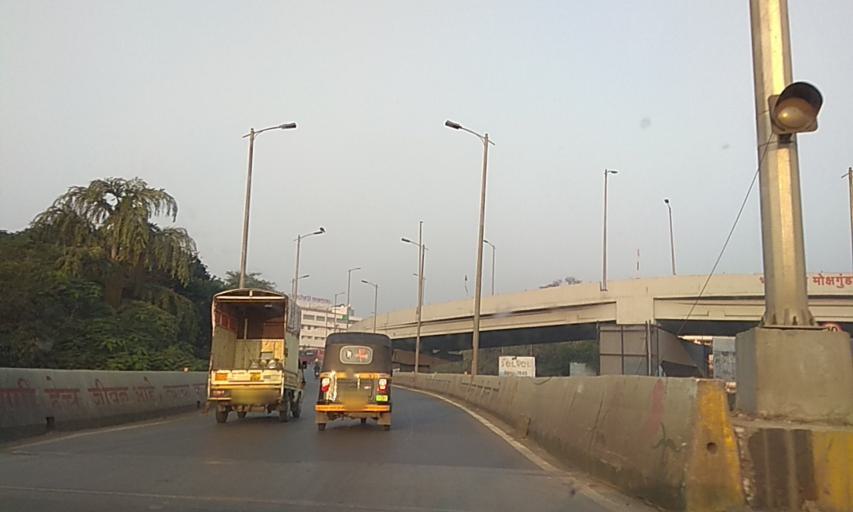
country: IN
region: Maharashtra
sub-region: Pune Division
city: Shivaji Nagar
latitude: 18.5301
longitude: 73.8554
